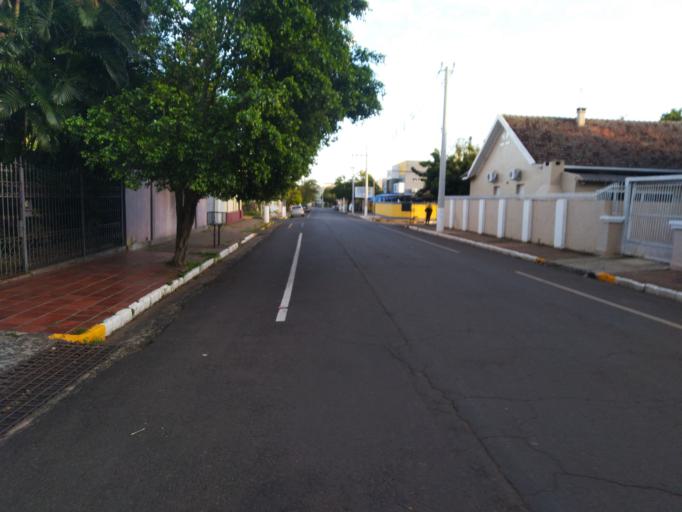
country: BR
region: Rio Grande do Sul
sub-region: Sao Borja
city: Sao Borja
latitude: -28.6516
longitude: -56.0068
